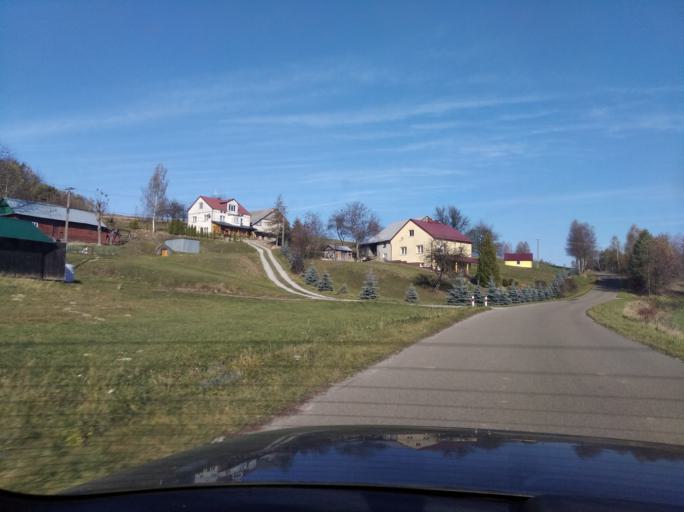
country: PL
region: Subcarpathian Voivodeship
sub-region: Powiat ropczycko-sedziszowski
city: Wielopole Skrzynskie
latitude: 49.9100
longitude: 21.5669
